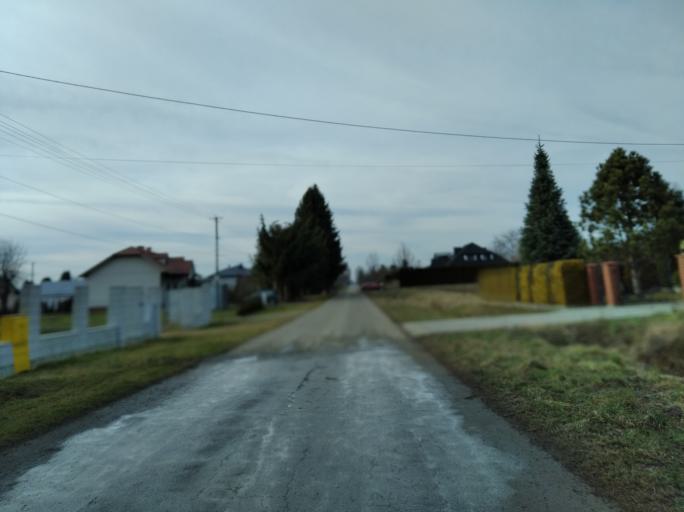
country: PL
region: Subcarpathian Voivodeship
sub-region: Powiat brzozowski
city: Turze Pole
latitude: 49.6599
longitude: 22.0128
